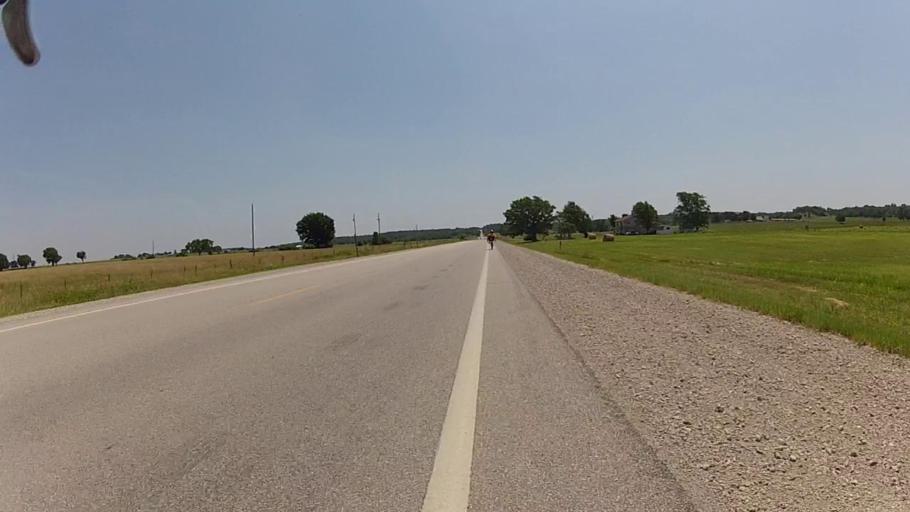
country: US
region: Kansas
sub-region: Montgomery County
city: Cherryvale
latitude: 37.2244
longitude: -95.5965
